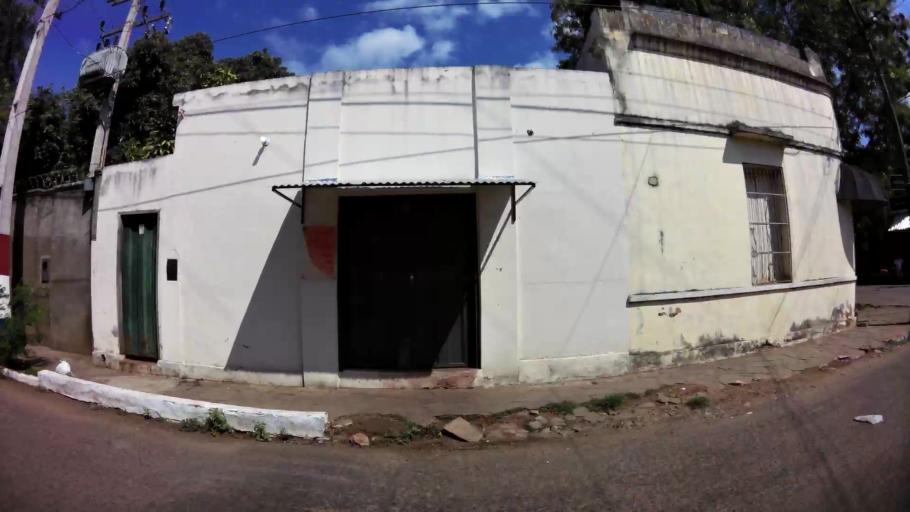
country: PY
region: Central
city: San Lorenzo
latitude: -25.3429
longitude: -57.5132
